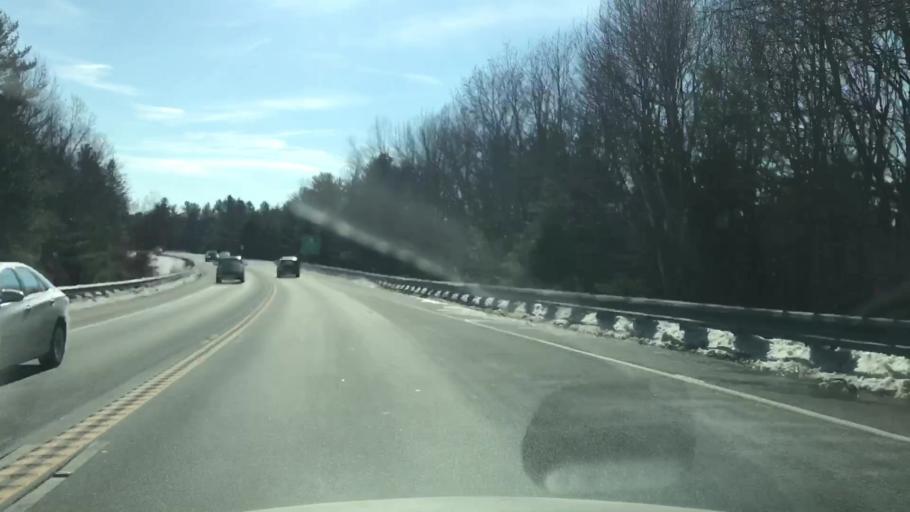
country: US
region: New Hampshire
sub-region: Hillsborough County
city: Milford
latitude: 42.8399
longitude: -71.6191
